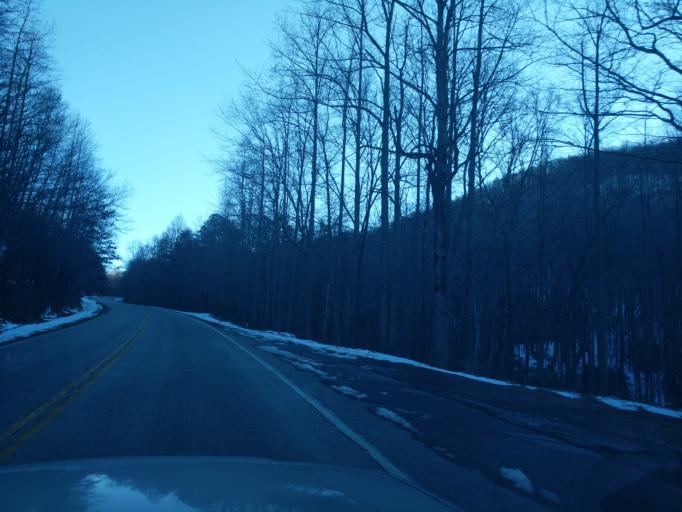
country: US
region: Georgia
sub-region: Towns County
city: Hiawassee
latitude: 34.9168
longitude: -83.6241
